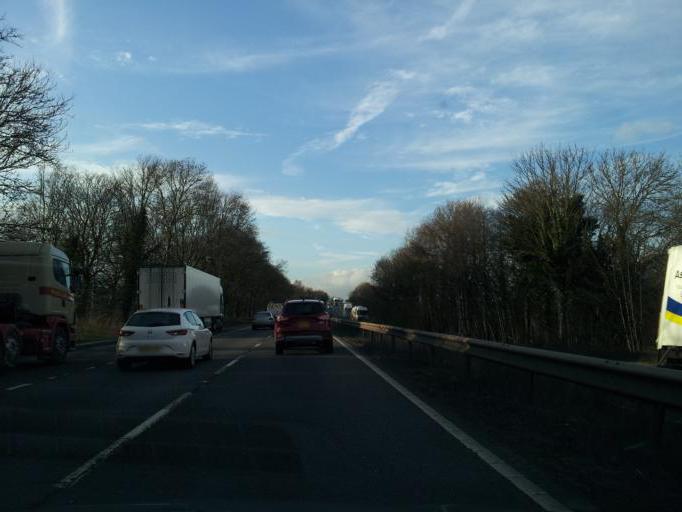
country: GB
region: England
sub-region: Peterborough
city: Thornhaugh
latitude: 52.6043
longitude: -0.4279
